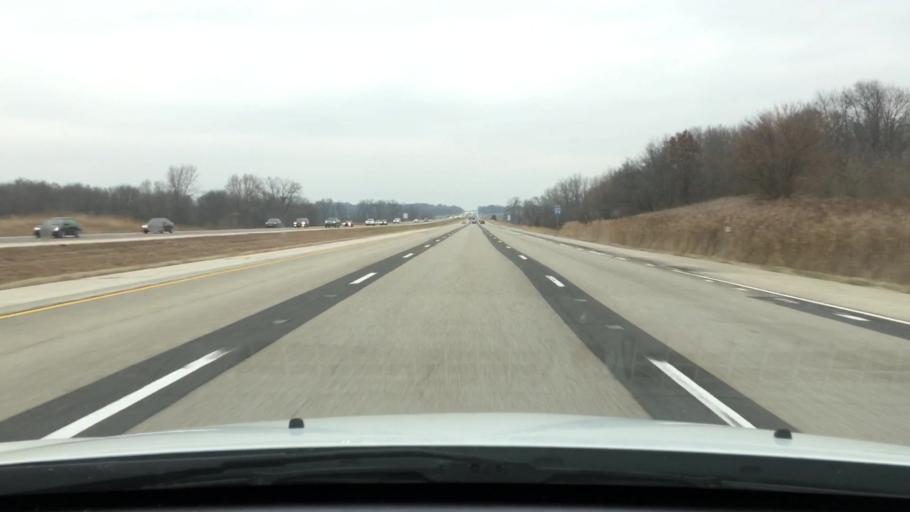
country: US
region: Illinois
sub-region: Logan County
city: Lincoln
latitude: 40.1187
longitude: -89.4164
